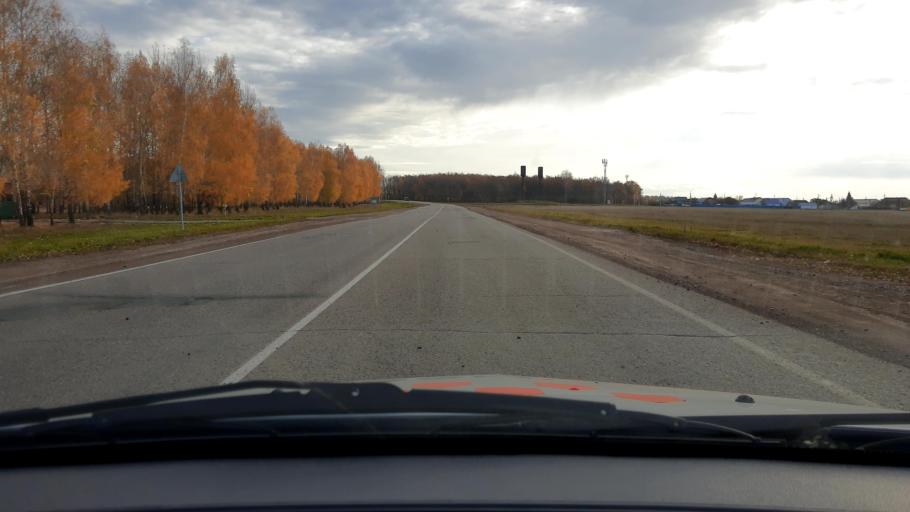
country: RU
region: Bashkortostan
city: Avdon
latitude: 54.8203
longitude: 55.7032
